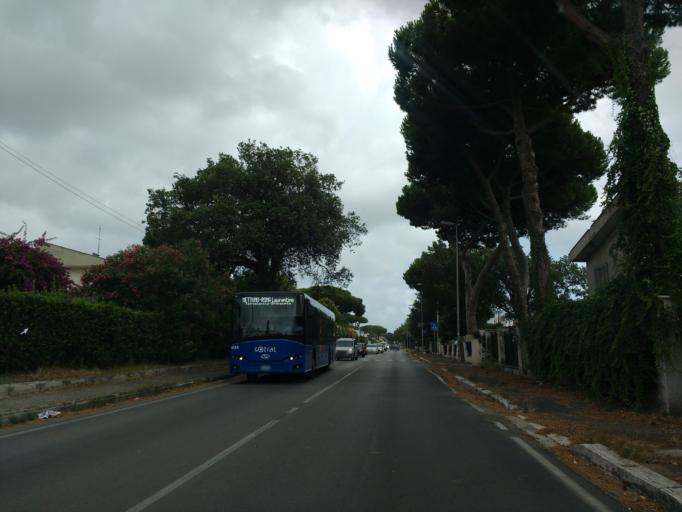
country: IT
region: Latium
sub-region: Citta metropolitana di Roma Capitale
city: Anzio
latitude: 41.4863
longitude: 12.6000
